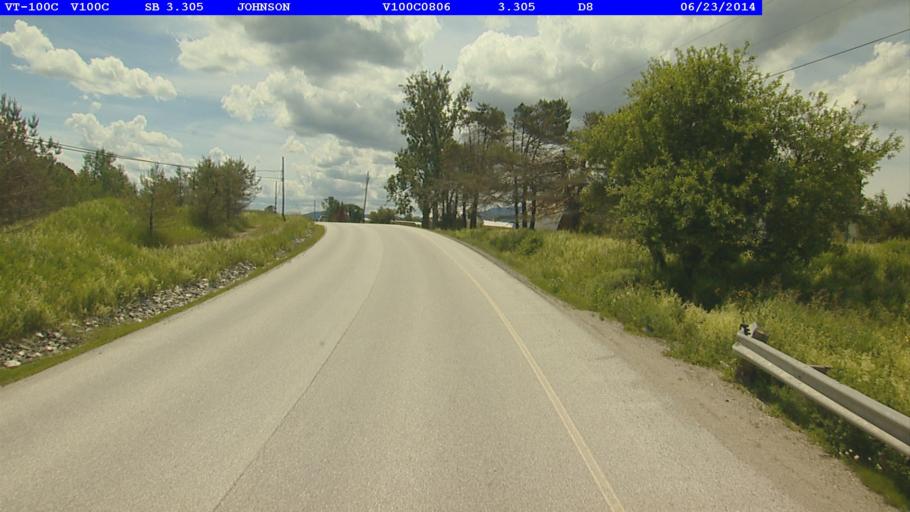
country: US
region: Vermont
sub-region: Lamoille County
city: Johnson
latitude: 44.6597
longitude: -72.6283
